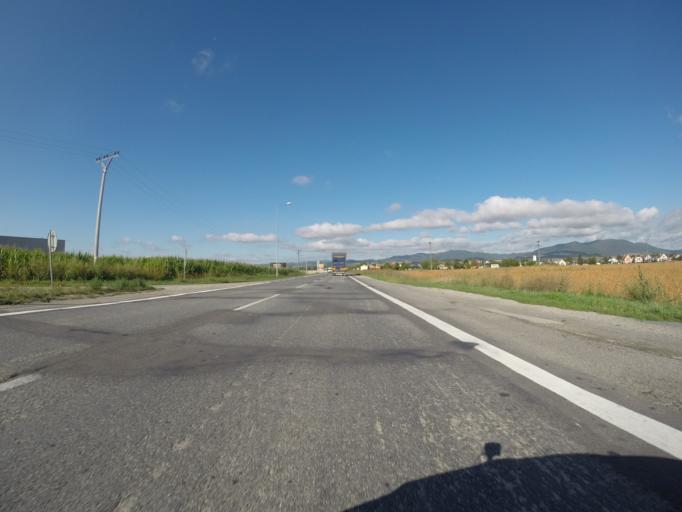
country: SK
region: Trenciansky
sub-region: Okres Trencin
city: Trencin
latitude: 48.8487
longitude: 17.9895
